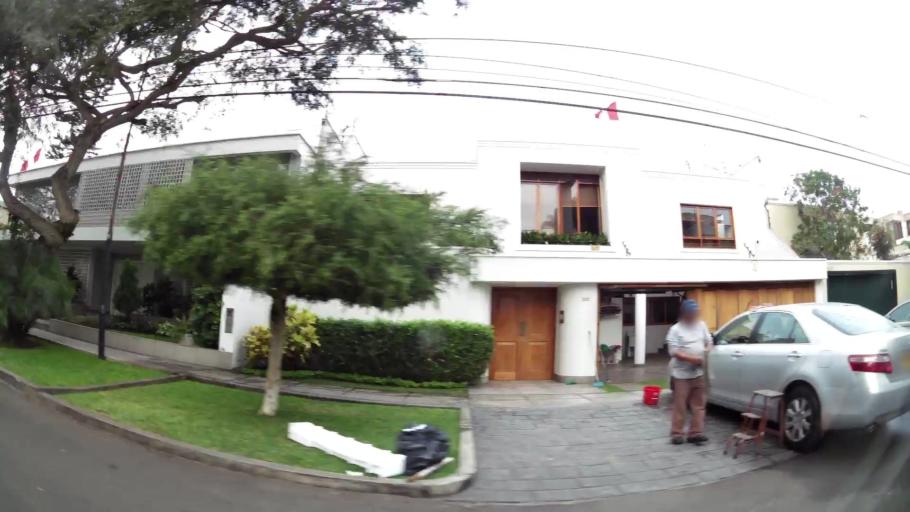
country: PE
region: Lima
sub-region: Lima
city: San Isidro
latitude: -12.1058
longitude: -77.0494
